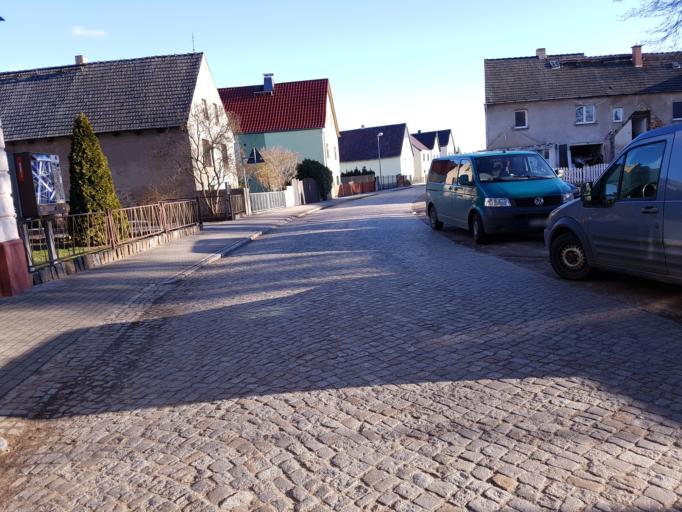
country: DE
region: Brandenburg
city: Groden
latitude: 51.4082
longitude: 13.5711
